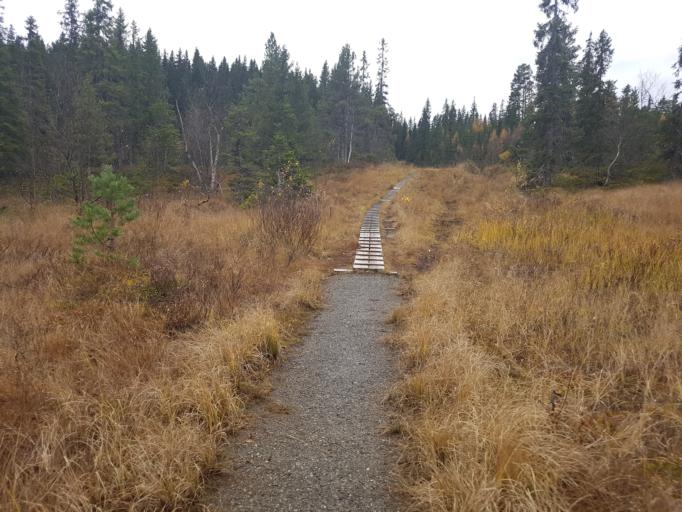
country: NO
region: Sor-Trondelag
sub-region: Melhus
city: Melhus
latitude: 63.3871
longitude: 10.2430
